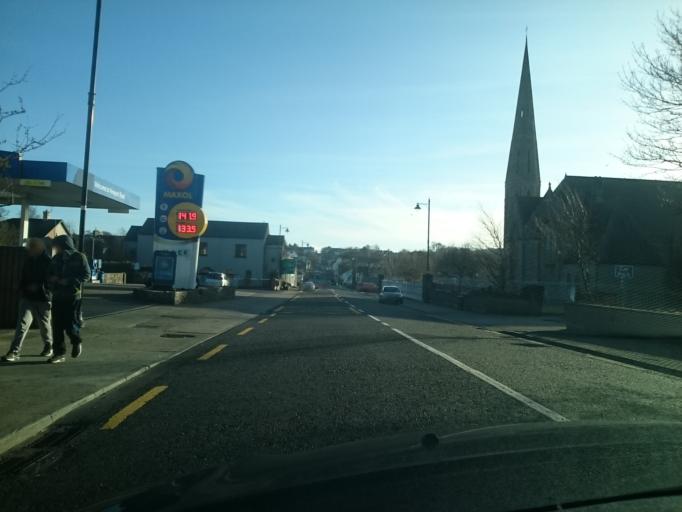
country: IE
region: Connaught
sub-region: Maigh Eo
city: Westport
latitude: 53.8024
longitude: -9.5207
